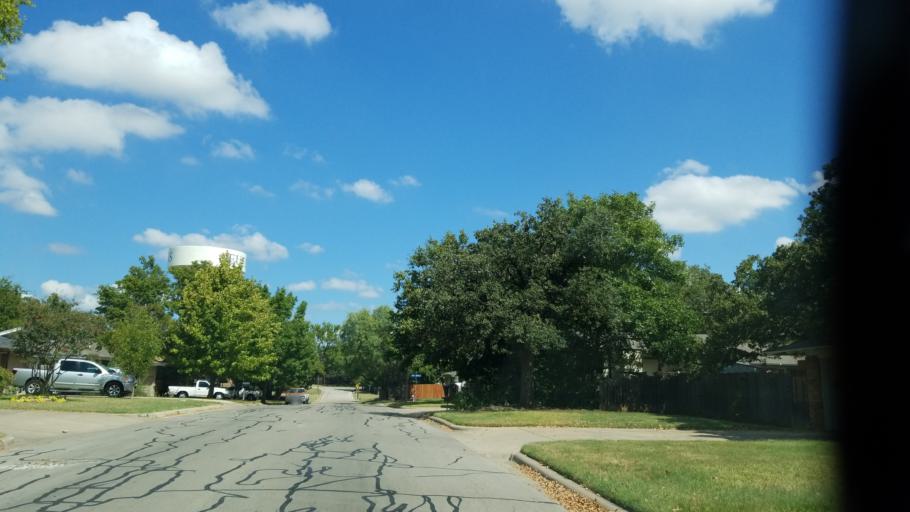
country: US
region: Texas
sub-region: Tarrant County
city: Euless
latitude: 32.8325
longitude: -97.0777
